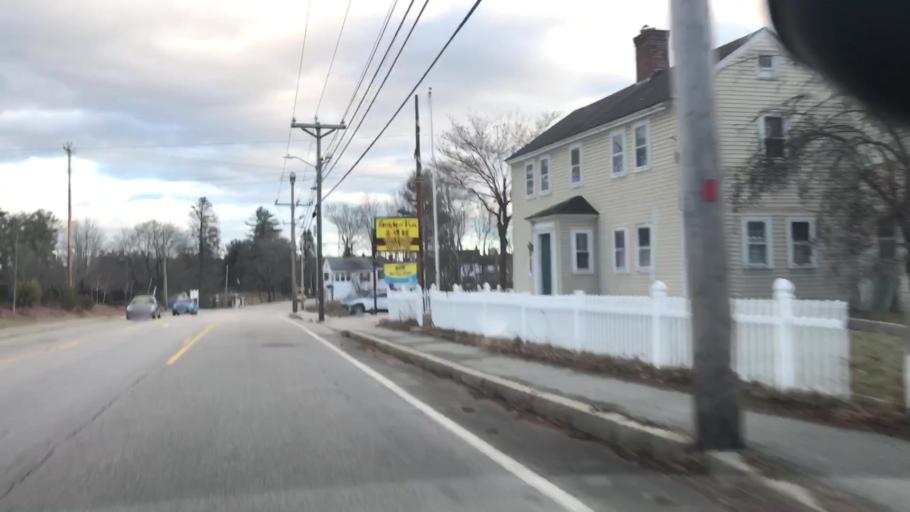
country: US
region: New Hampshire
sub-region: Hillsborough County
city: Milford
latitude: 42.8292
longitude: -71.6345
